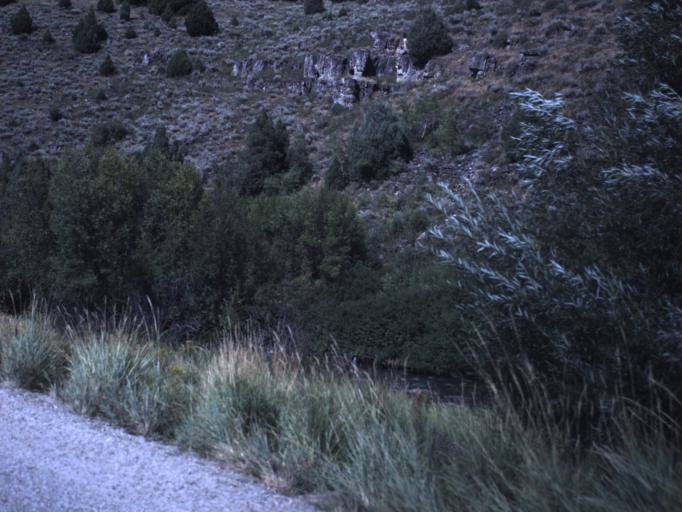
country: US
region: Utah
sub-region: Cache County
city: North Logan
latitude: 41.8508
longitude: -111.5844
